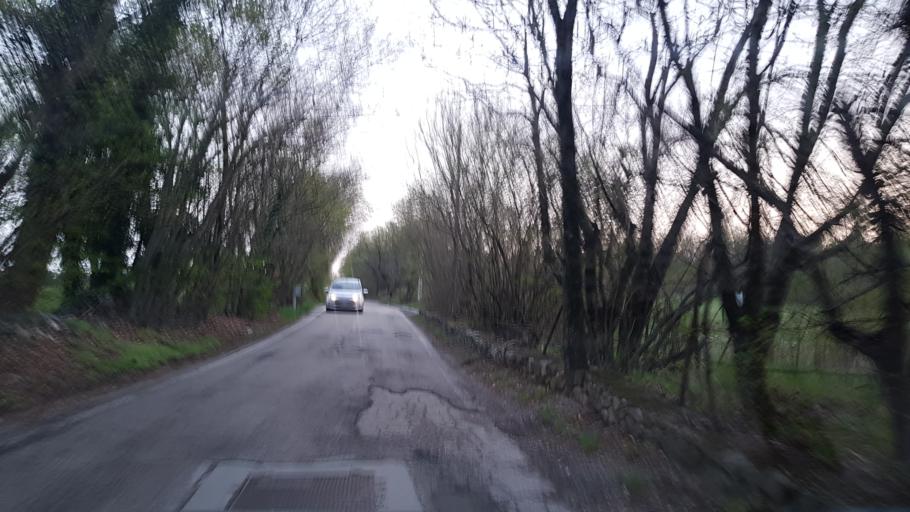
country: IT
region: Friuli Venezia Giulia
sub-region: Provincia di Trieste
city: Domio
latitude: 45.6454
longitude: 13.8365
